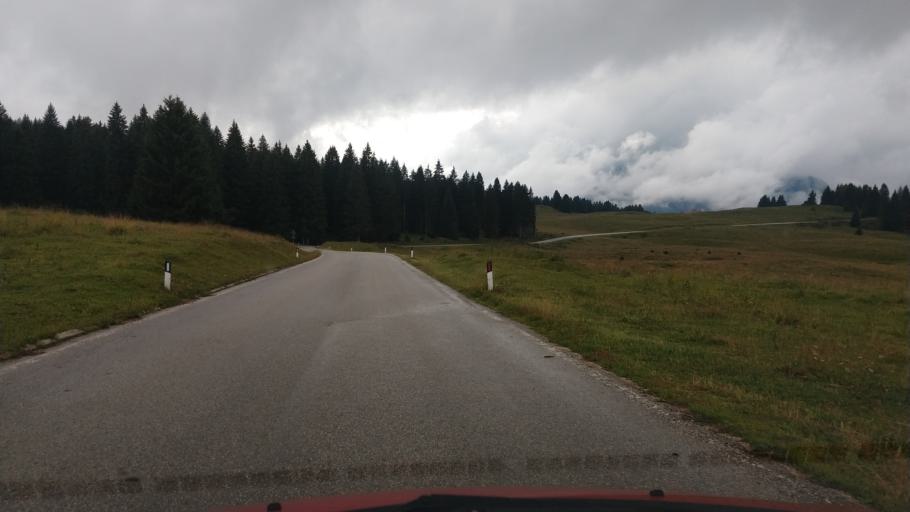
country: IT
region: Veneto
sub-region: Provincia di Vicenza
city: Lastebasse
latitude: 45.9053
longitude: 11.2455
